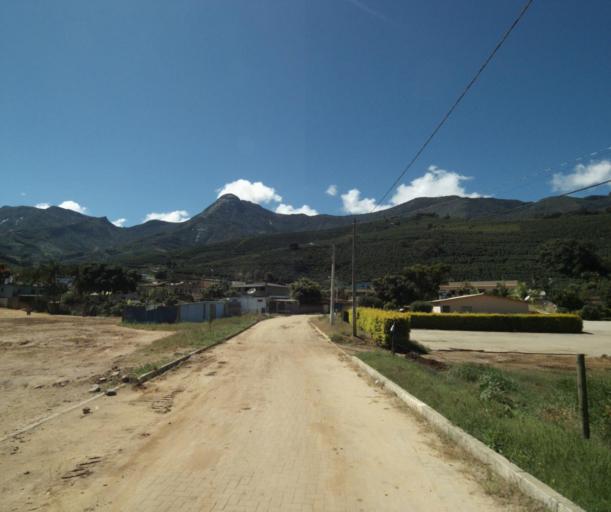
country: BR
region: Minas Gerais
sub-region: Espera Feliz
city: Espera Feliz
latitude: -20.5547
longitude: -41.8197
